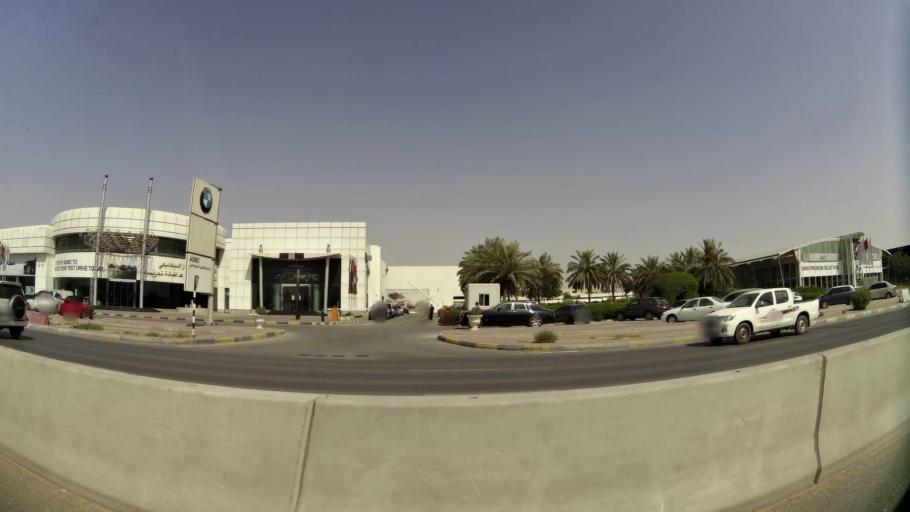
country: AE
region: Ash Shariqah
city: Sharjah
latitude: 25.3189
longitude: 55.4282
